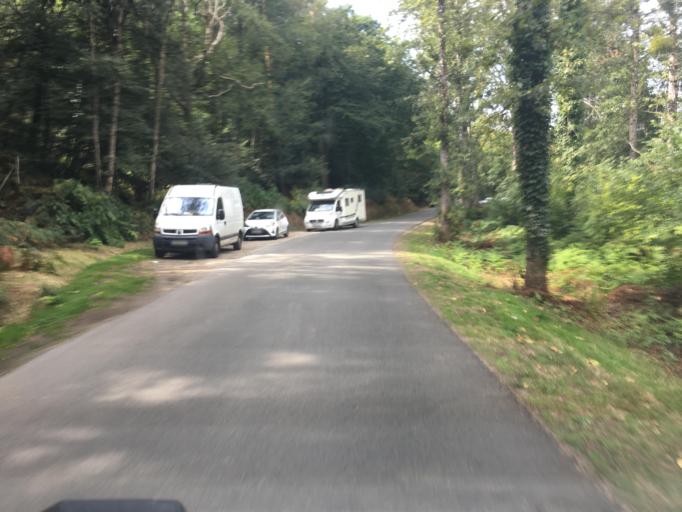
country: FR
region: Brittany
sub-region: Departement des Cotes-d'Armor
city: Gouarec
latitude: 48.2104
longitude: -3.1280
